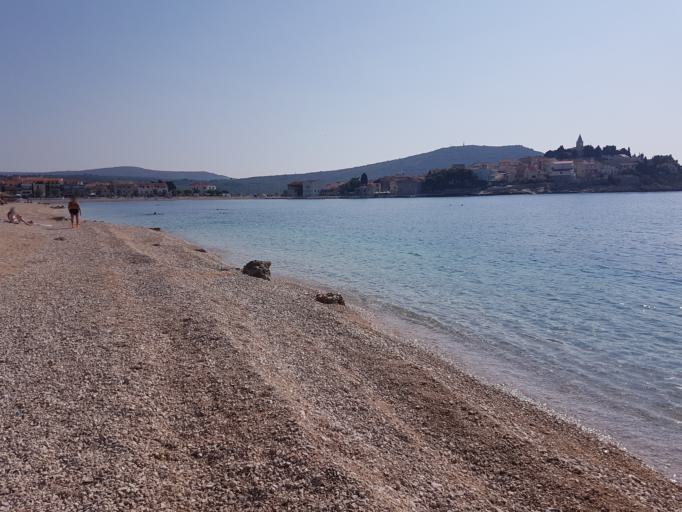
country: HR
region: Sibensko-Kniniska
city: Primosten
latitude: 43.5893
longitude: 15.9192
